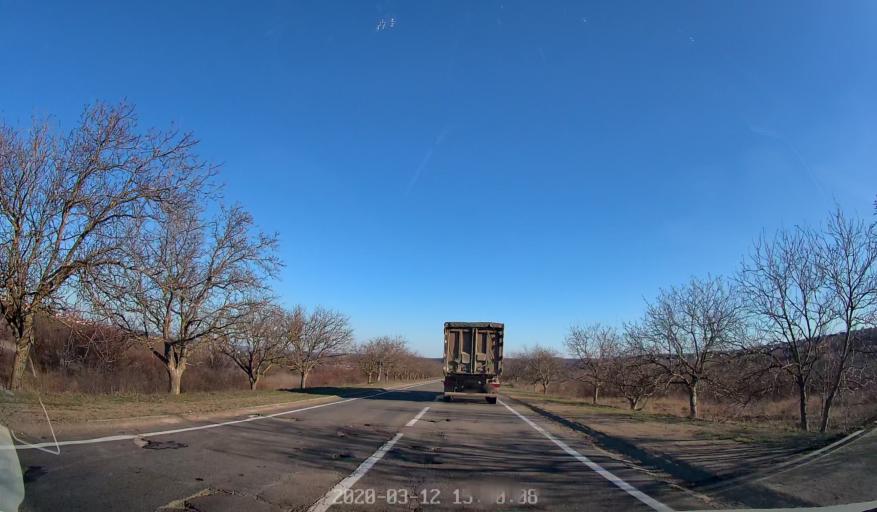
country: MD
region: Chisinau
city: Ciorescu
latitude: 47.0758
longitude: 28.9513
